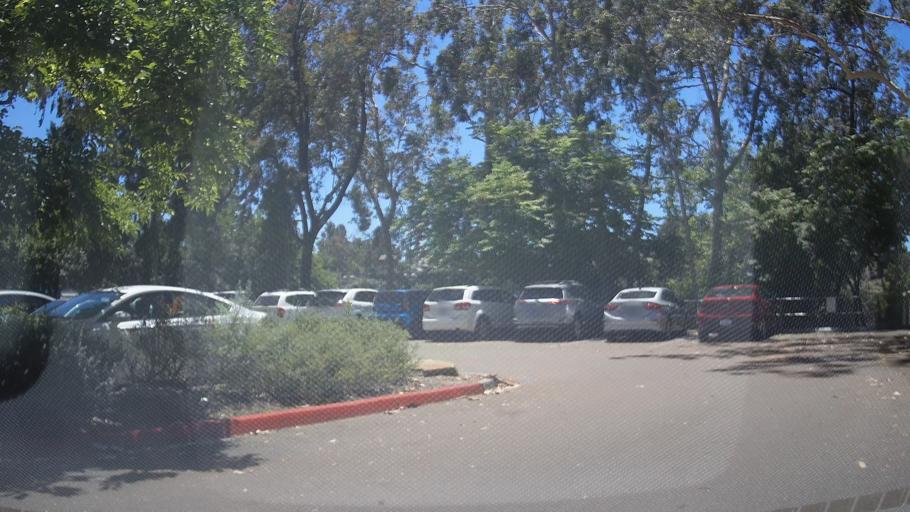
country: US
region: California
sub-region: San Diego County
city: La Mesa
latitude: 32.7894
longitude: -117.0050
